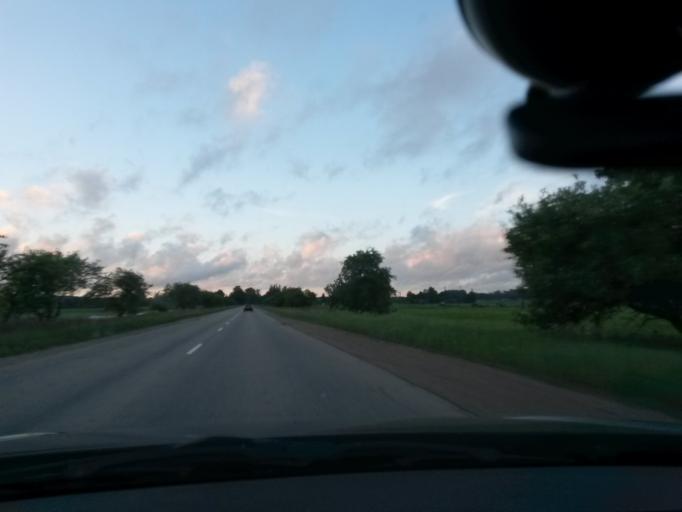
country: LV
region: Jekabpils Rajons
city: Jekabpils
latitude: 56.7155
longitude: 25.9878
